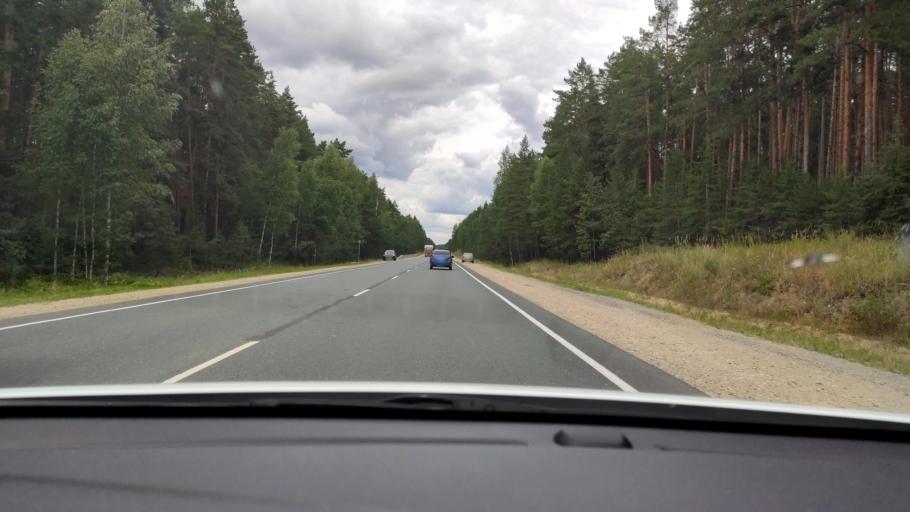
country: RU
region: Mariy-El
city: Pomary
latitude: 56.0376
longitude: 48.3796
